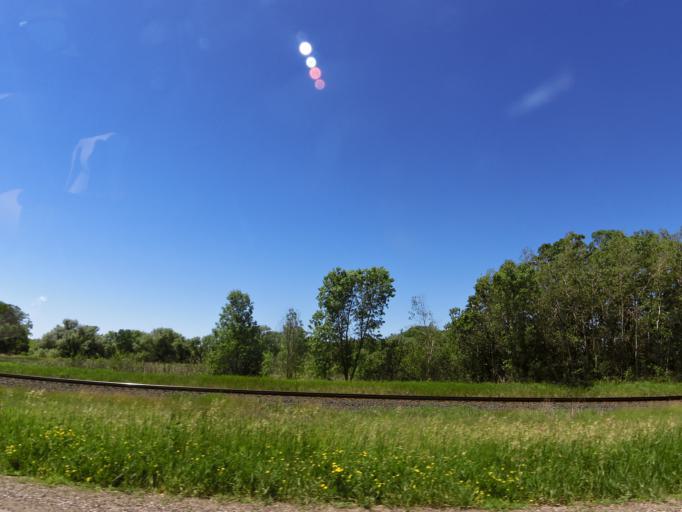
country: US
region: Minnesota
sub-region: Becker County
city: Detroit Lakes
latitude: 46.8666
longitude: -95.8890
